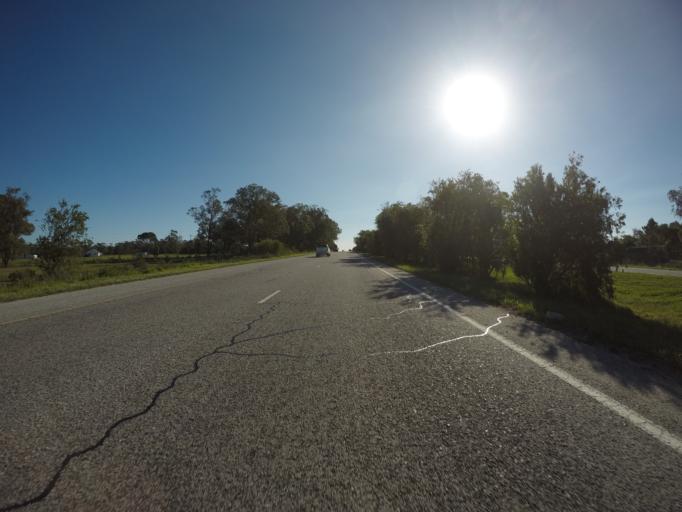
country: ZA
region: Eastern Cape
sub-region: Nelson Mandela Bay Metropolitan Municipality
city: Uitenhage
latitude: -33.9365
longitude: 25.3673
